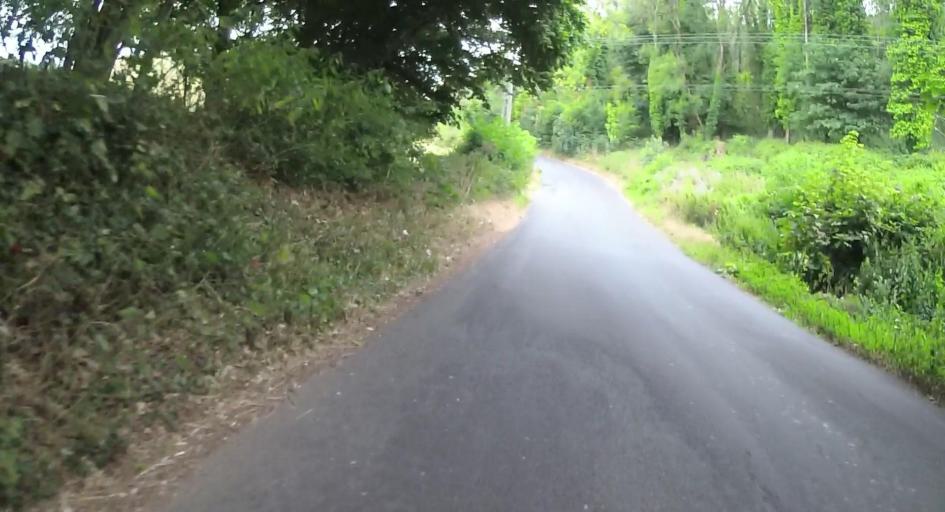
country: GB
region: England
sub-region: Dorset
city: Swanage
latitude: 50.6329
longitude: -1.9813
